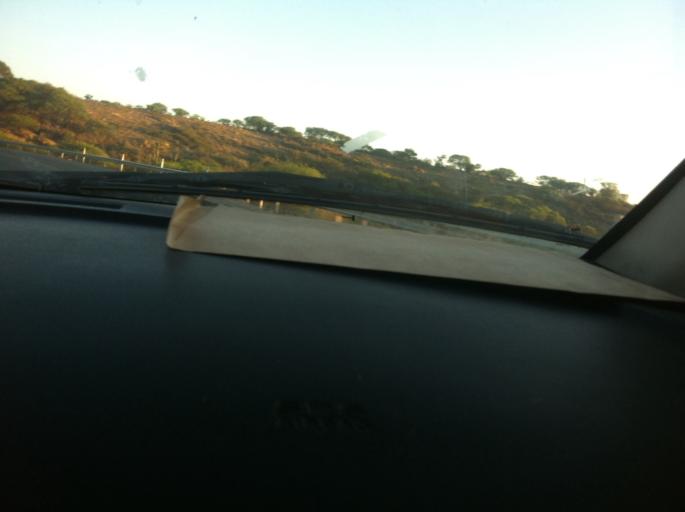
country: BO
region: Cochabamba
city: Capinota
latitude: -17.5932
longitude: -66.3452
